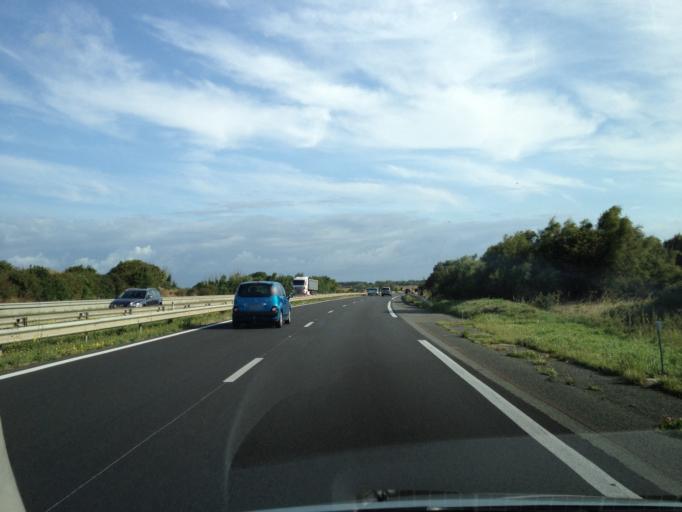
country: FR
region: Poitou-Charentes
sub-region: Departement de la Charente-Maritime
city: Yves
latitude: 46.0280
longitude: -1.0558
